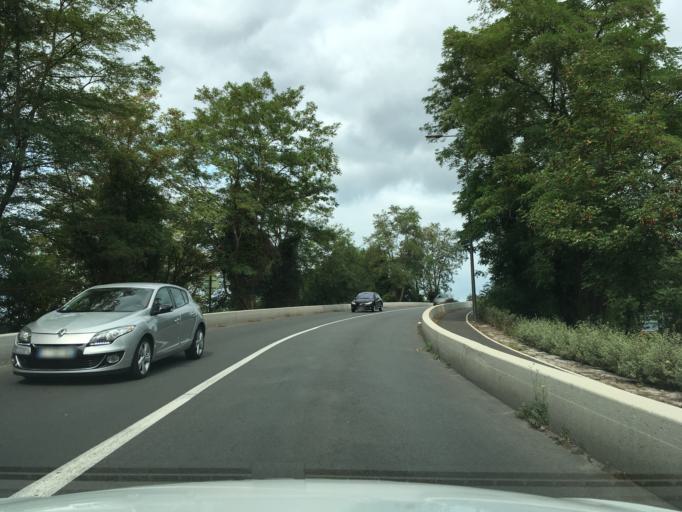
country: FR
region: Aquitaine
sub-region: Departement des Pyrenees-Atlantiques
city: Mouguerre
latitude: 43.4826
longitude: -1.4446
